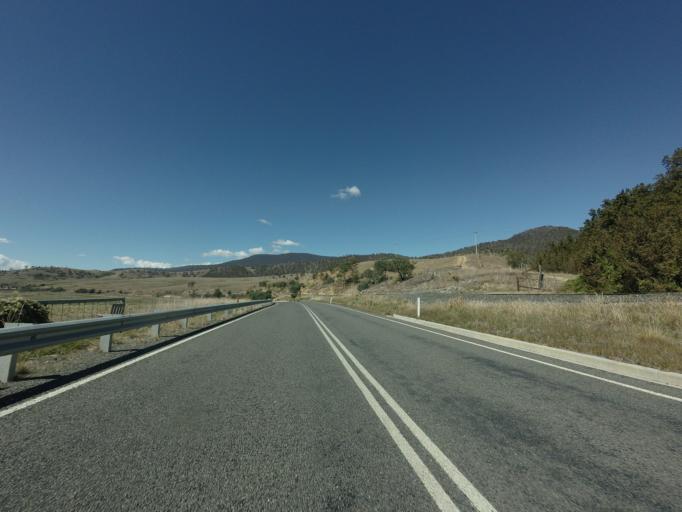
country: AU
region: Tasmania
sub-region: Northern Midlands
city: Evandale
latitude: -41.7346
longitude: 147.8145
